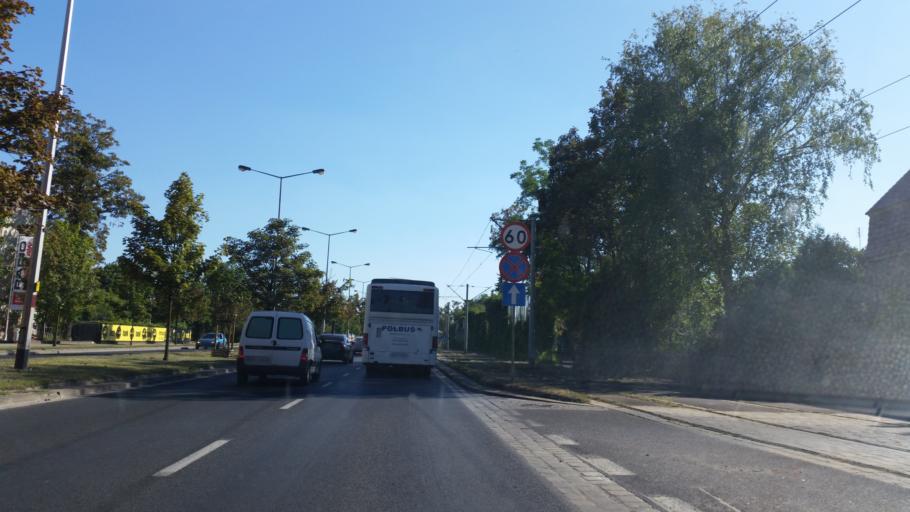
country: PL
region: Lower Silesian Voivodeship
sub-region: Powiat wroclawski
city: Wroclaw
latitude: 51.0714
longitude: 17.0059
